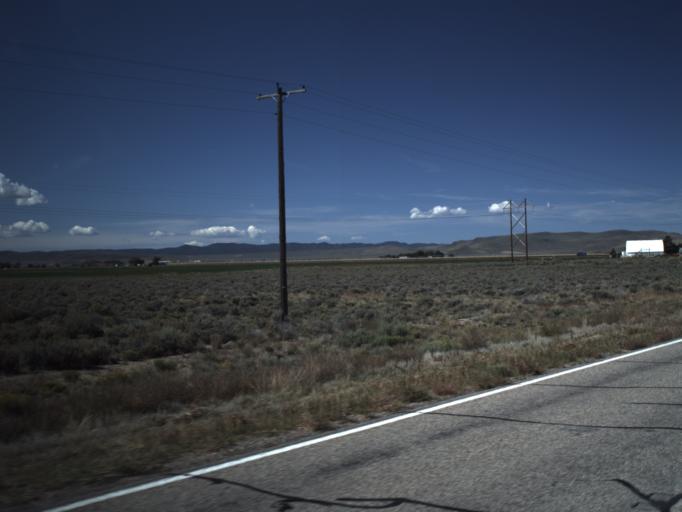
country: US
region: Utah
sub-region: Washington County
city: Enterprise
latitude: 37.7056
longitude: -113.6454
